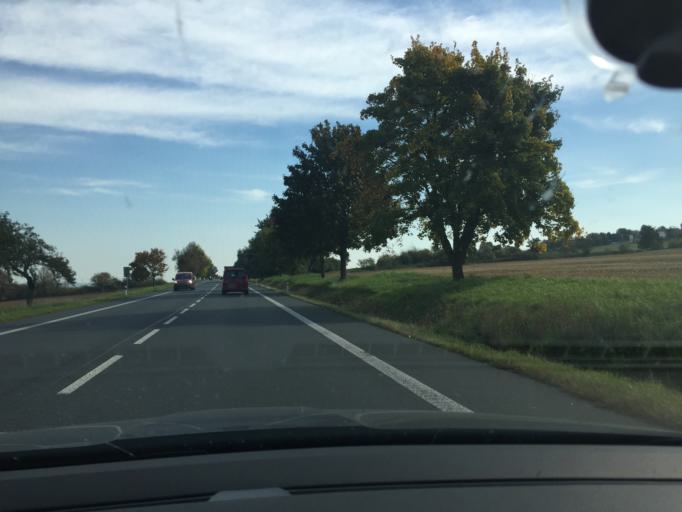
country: CZ
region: Central Bohemia
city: Velim
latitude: 50.0377
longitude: 15.1244
